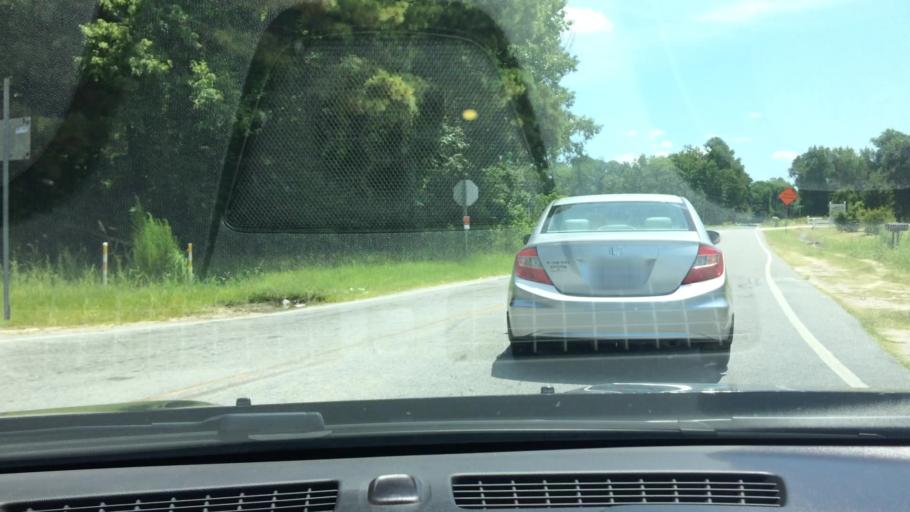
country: US
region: North Carolina
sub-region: Beaufort County
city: Washington
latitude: 35.6002
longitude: -77.1577
